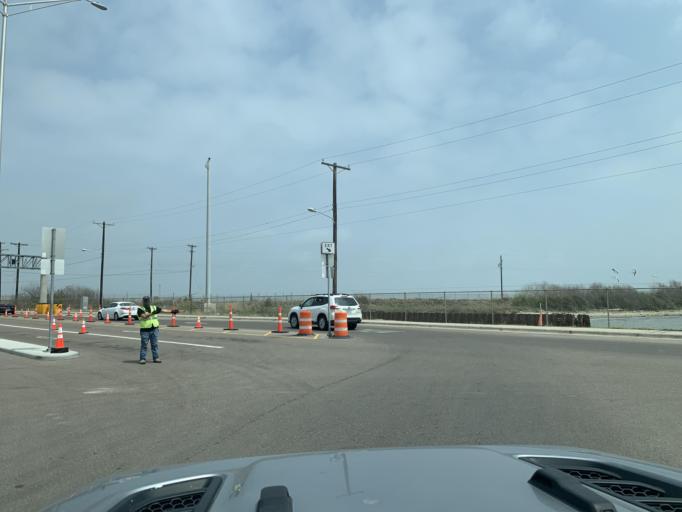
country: US
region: Texas
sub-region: Nueces County
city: Port Aransas
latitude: 27.8441
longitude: -97.0702
